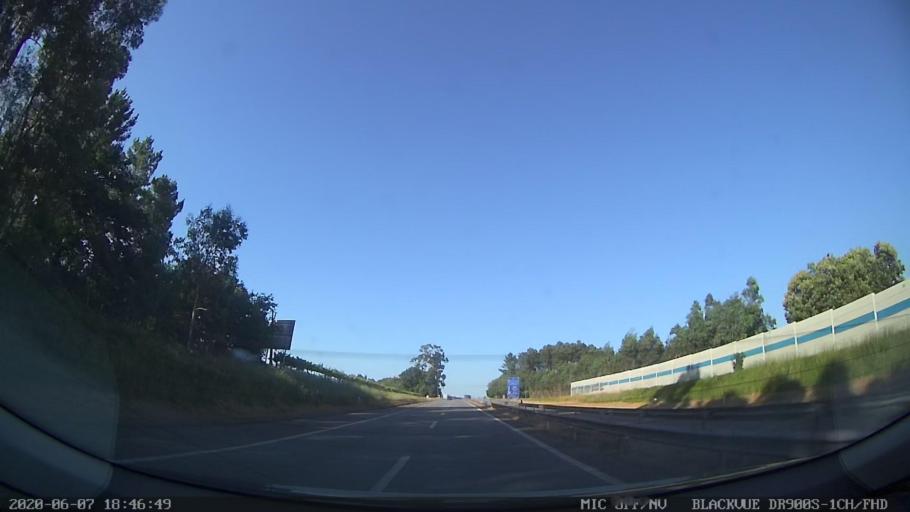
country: PT
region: Braga
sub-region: Vila Nova de Famalicao
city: Vila Nova de Famalicao
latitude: 41.3970
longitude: -8.4699
